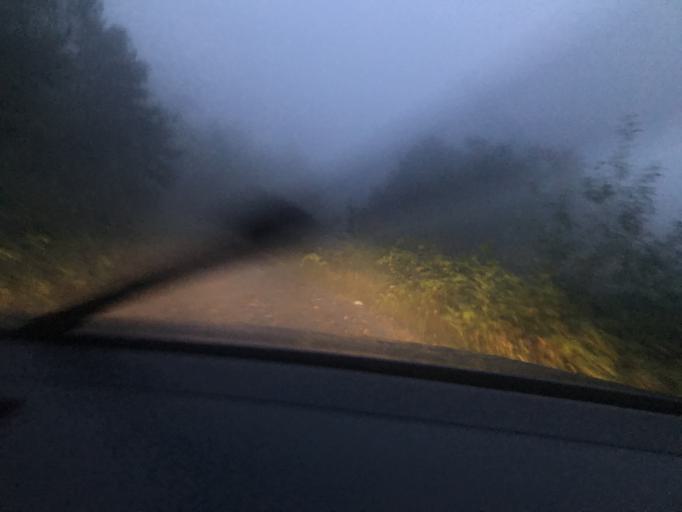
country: TR
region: Trabzon
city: Hayrat
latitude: 40.8303
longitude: 40.3878
